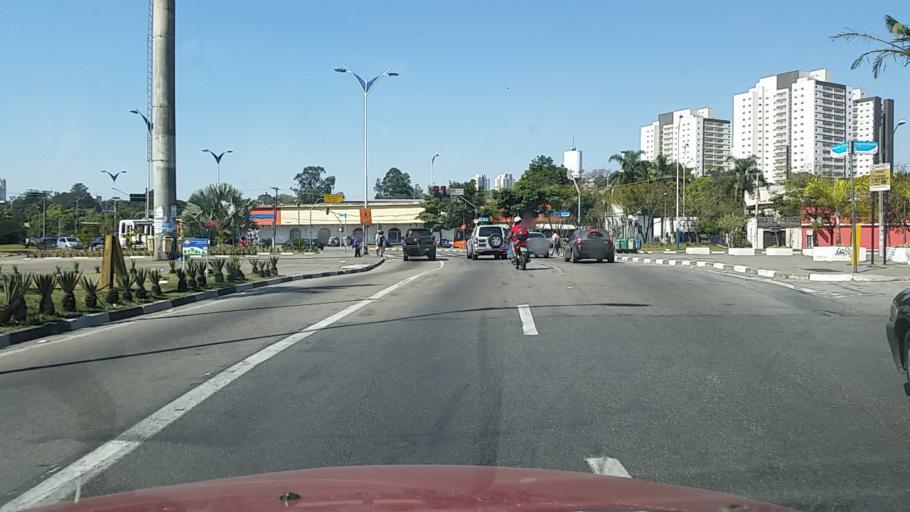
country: BR
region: Sao Paulo
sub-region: Taboao Da Serra
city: Taboao da Serra
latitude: -23.6078
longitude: -46.7523
